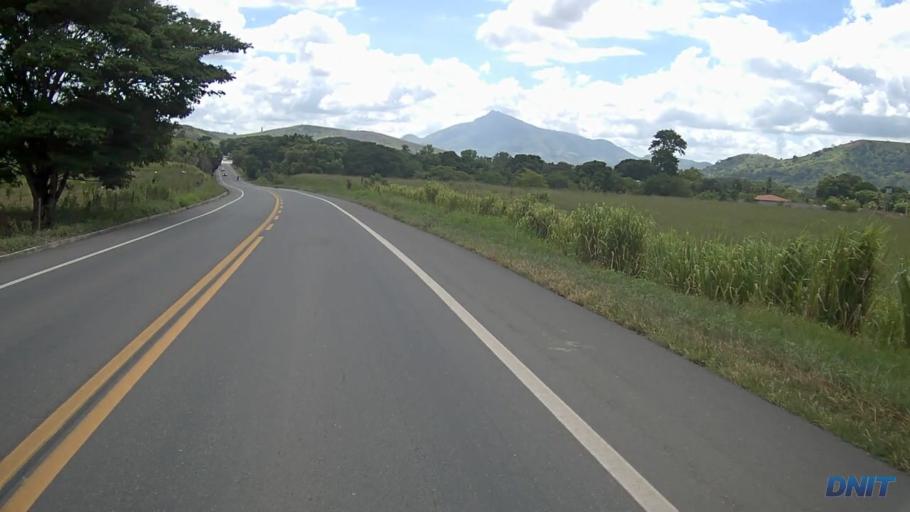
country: BR
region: Minas Gerais
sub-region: Governador Valadares
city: Governador Valadares
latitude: -18.9423
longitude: -42.0599
